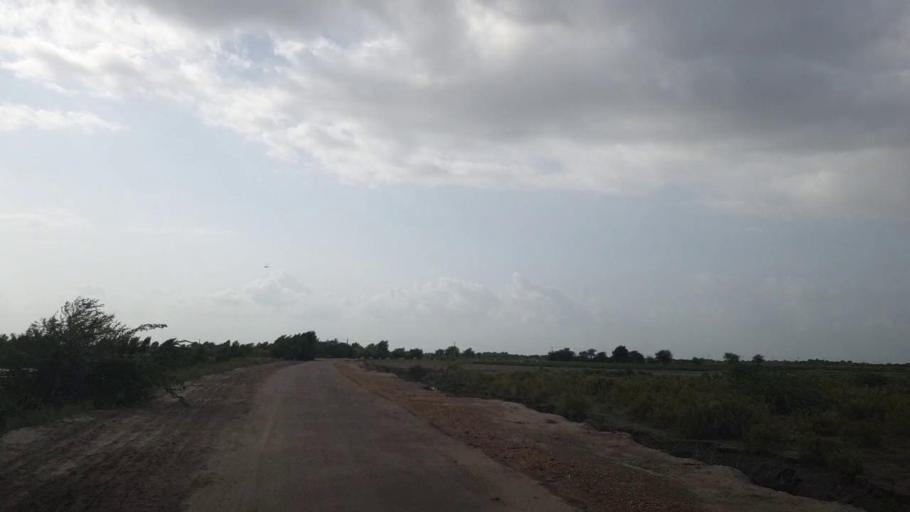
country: PK
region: Sindh
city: Kadhan
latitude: 24.5849
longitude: 69.0568
